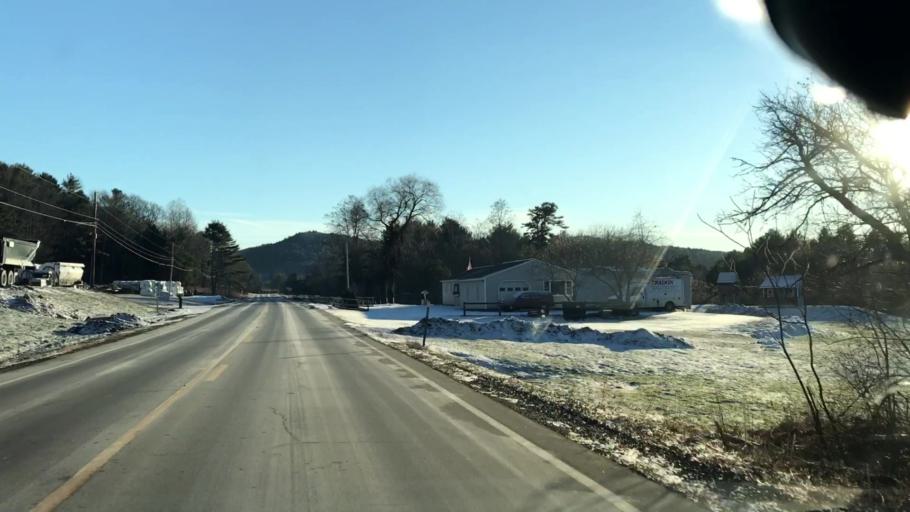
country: US
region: New Hampshire
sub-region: Grafton County
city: Lyme Town Offices
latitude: 43.8557
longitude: -72.1556
